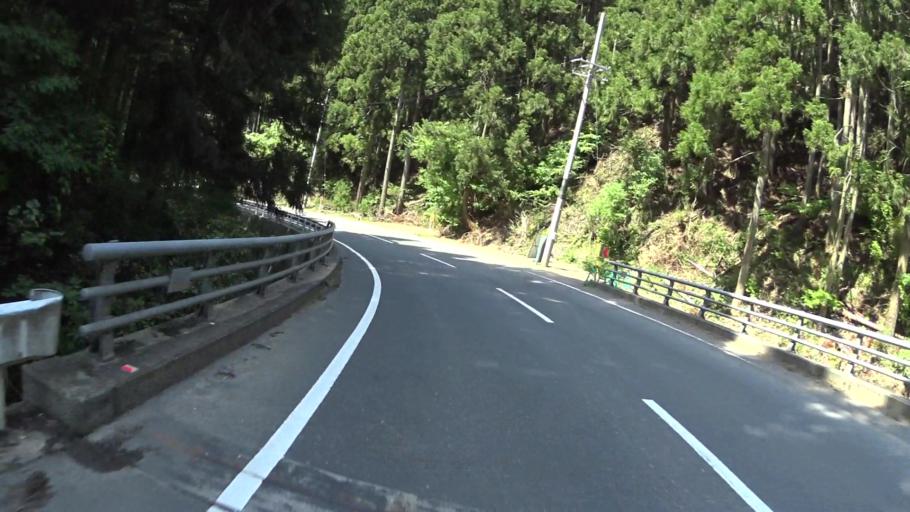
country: JP
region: Kyoto
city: Kameoka
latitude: 35.1245
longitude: 135.5586
